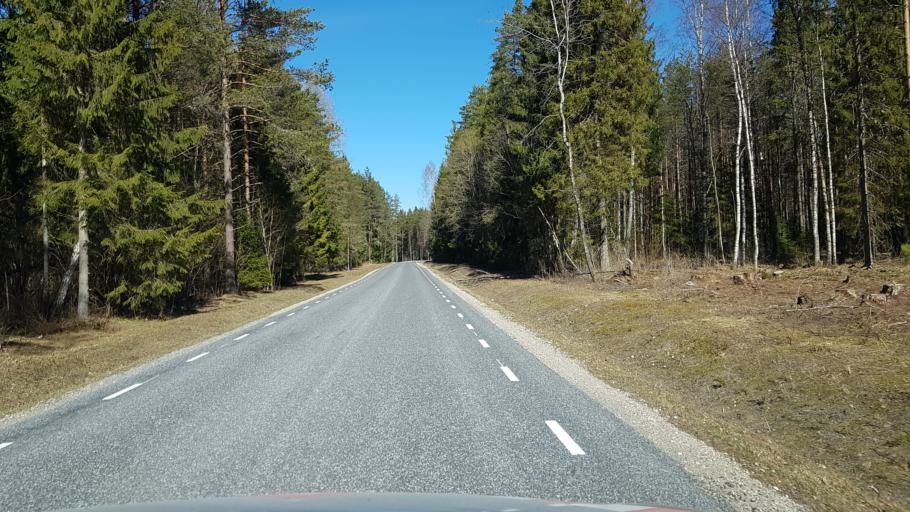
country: EE
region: Laeaene-Virumaa
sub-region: Vinni vald
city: Vinni
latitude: 59.1274
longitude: 26.5211
